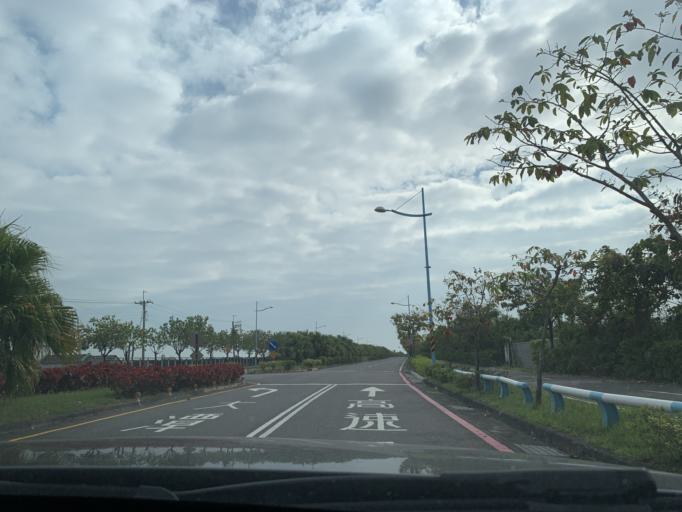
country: TW
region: Taiwan
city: Fengshan
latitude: 22.4519
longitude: 120.4877
